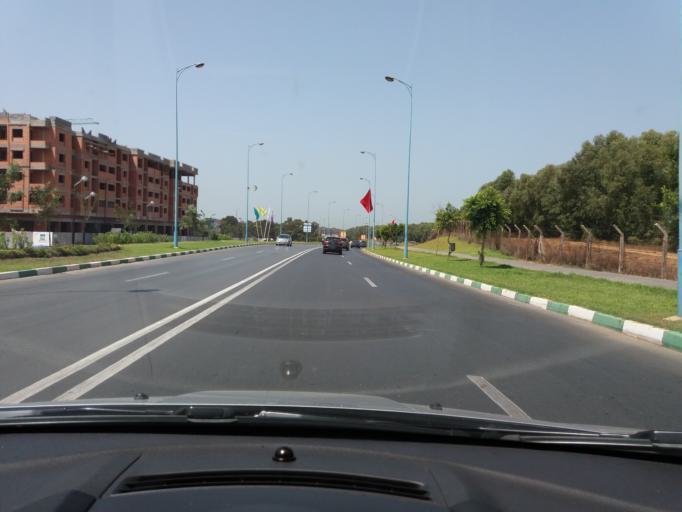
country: MA
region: Gharb-Chrarda-Beni Hssen
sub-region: Kenitra Province
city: Kenitra
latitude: 34.2719
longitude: -6.6285
